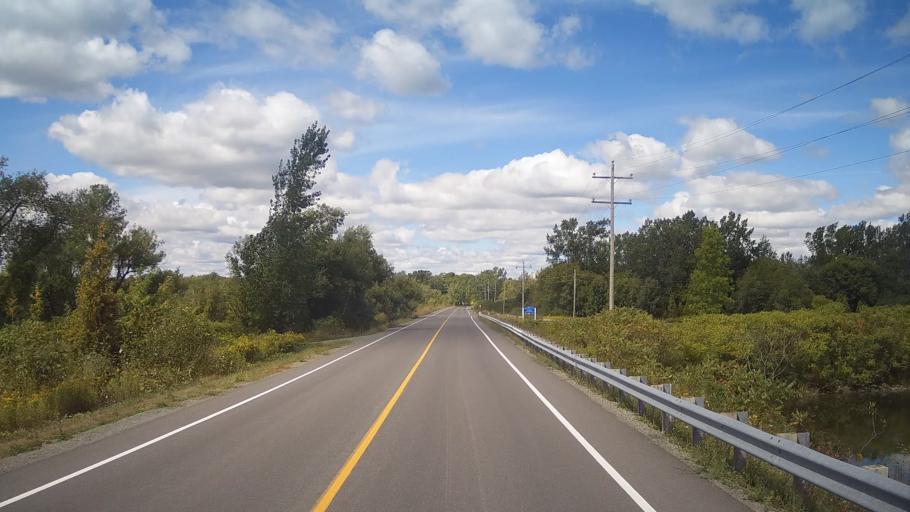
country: US
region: New York
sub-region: St. Lawrence County
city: Ogdensburg
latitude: 44.8349
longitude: -75.3150
